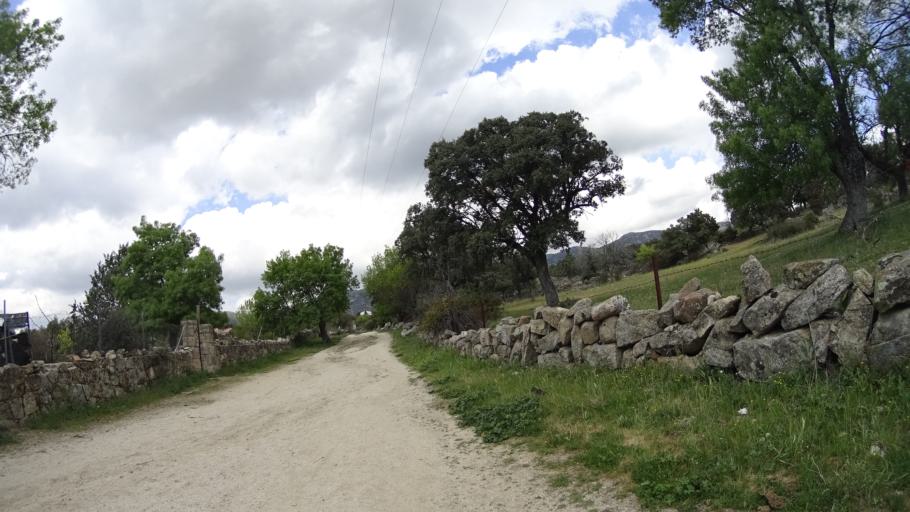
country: ES
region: Madrid
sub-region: Provincia de Madrid
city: Hoyo de Manzanares
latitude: 40.6195
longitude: -3.9017
